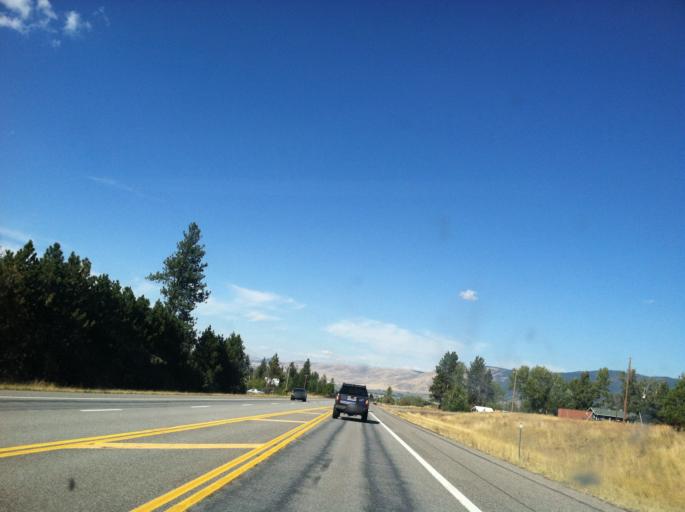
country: US
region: Montana
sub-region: Missoula County
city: Frenchtown
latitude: 47.0955
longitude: -114.0412
